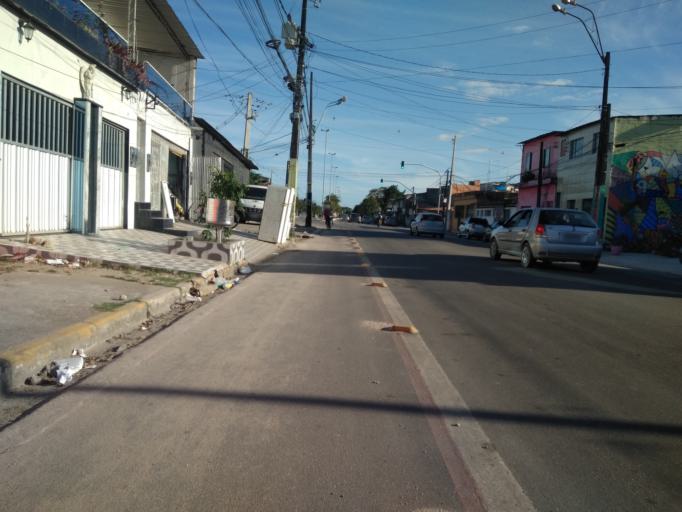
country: BR
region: Pernambuco
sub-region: Recife
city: Recife
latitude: -8.0746
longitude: -34.9301
